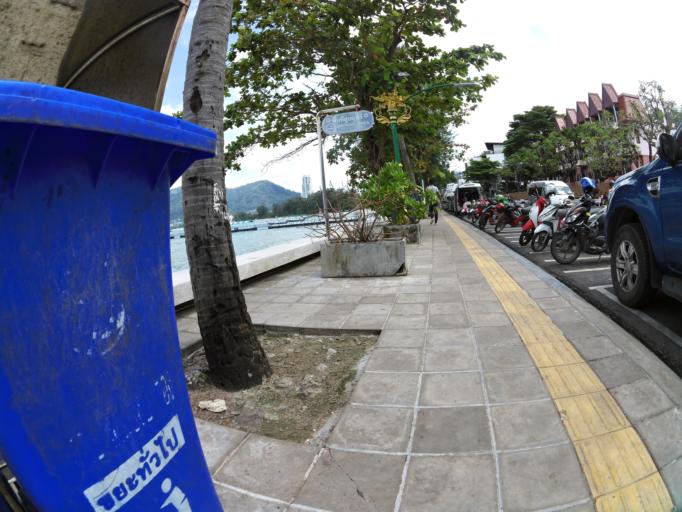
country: TH
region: Phuket
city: Patong
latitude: 7.8857
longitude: 98.2882
